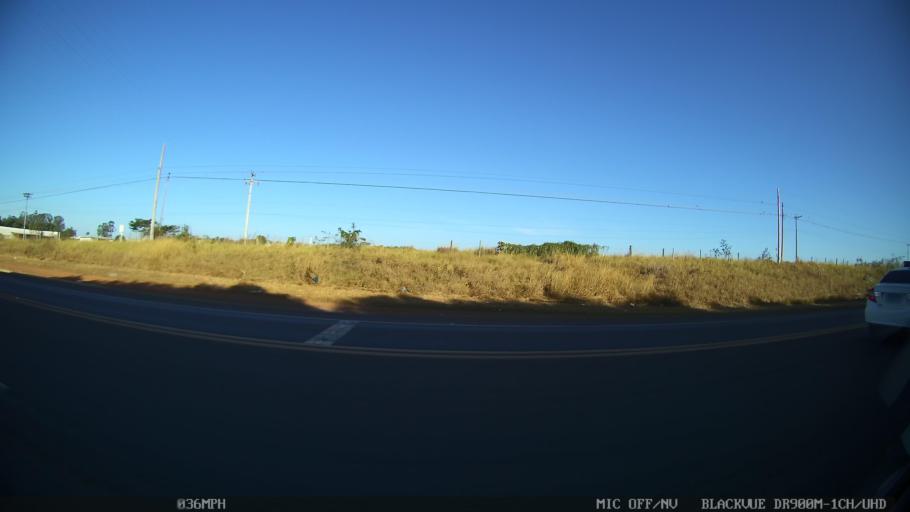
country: BR
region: Sao Paulo
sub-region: Olimpia
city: Olimpia
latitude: -20.6927
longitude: -48.9218
